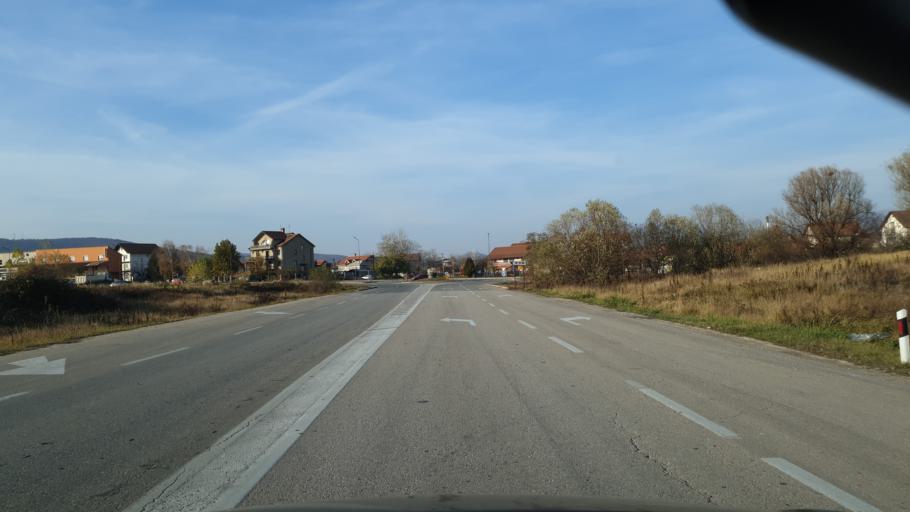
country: RS
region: Central Serbia
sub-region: Borski Okrug
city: Bor
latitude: 44.0570
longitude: 22.1114
